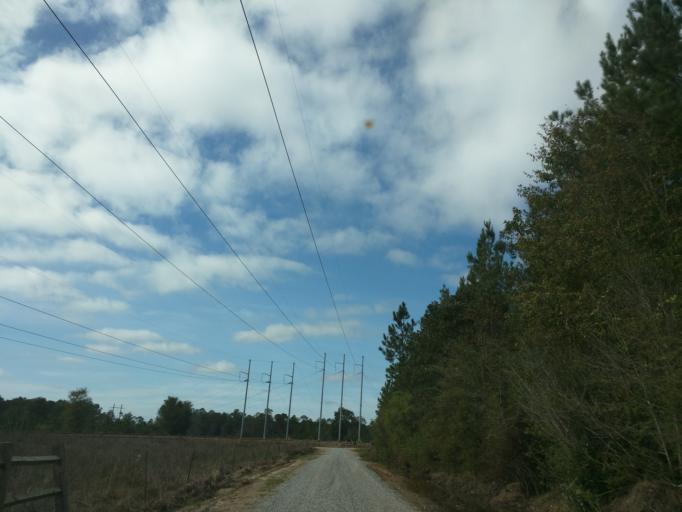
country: US
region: Florida
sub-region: Escambia County
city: Cantonment
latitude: 30.5333
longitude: -87.4353
